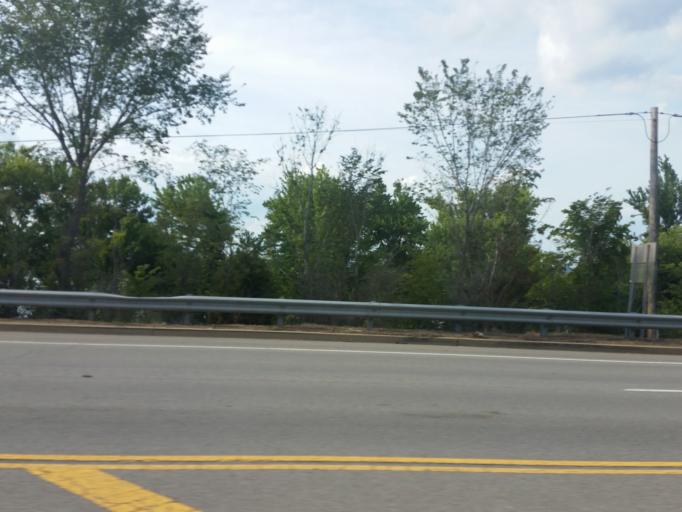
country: US
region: Tennessee
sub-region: Humphreys County
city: New Johnsonville
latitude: 36.0178
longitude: -87.9963
